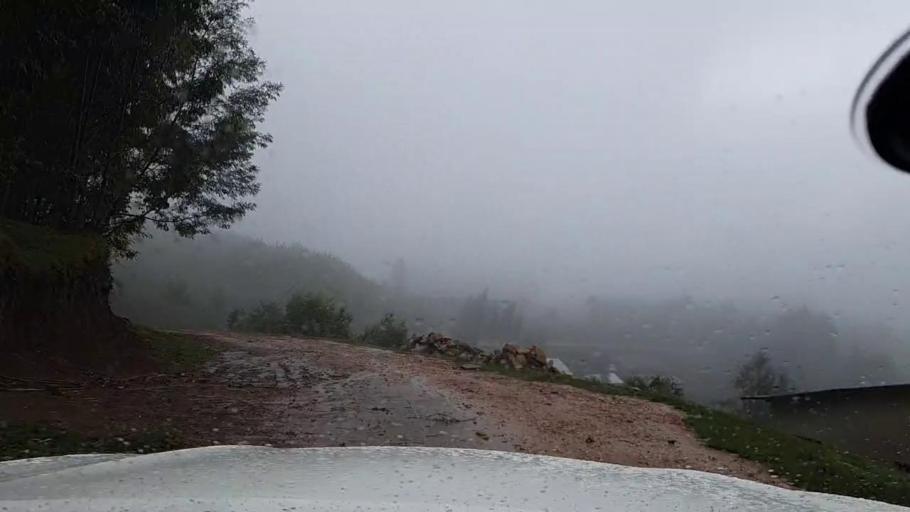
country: RW
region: Western Province
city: Kibuye
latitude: -2.1359
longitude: 29.4679
